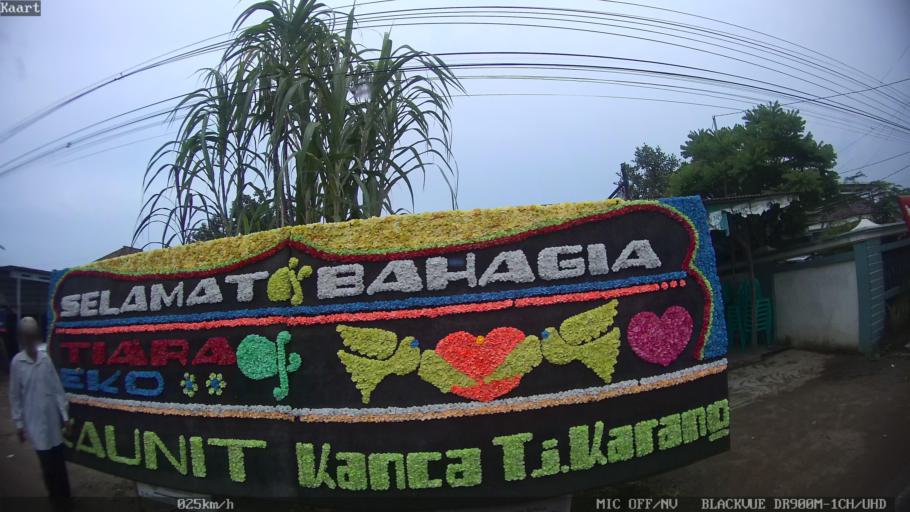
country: ID
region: Lampung
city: Kedaton
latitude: -5.3865
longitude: 105.2445
